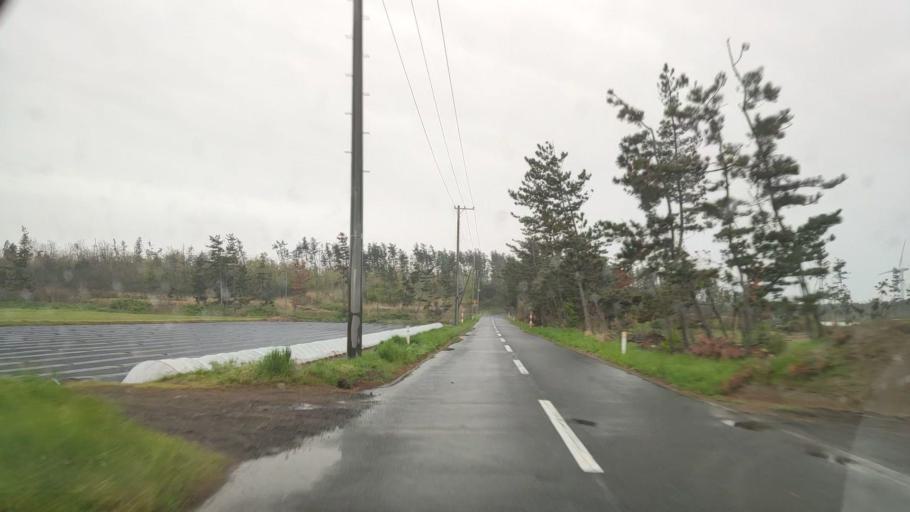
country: JP
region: Akita
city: Noshiromachi
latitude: 40.0964
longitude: 139.9659
